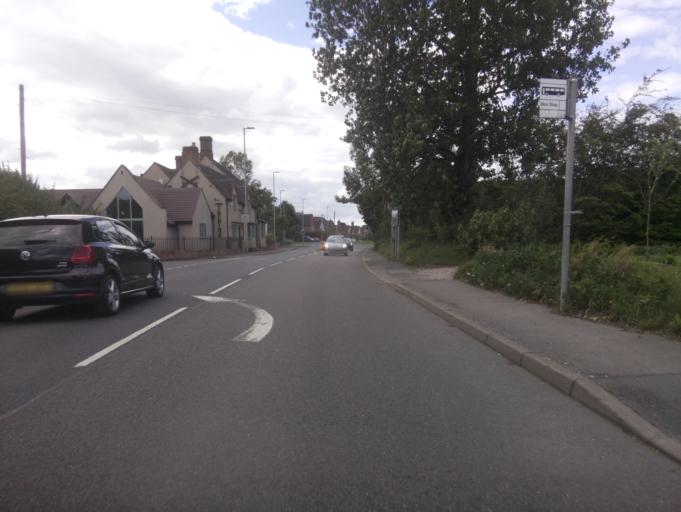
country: GB
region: England
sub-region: Leicestershire
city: Measham
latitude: 52.6422
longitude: -1.5050
